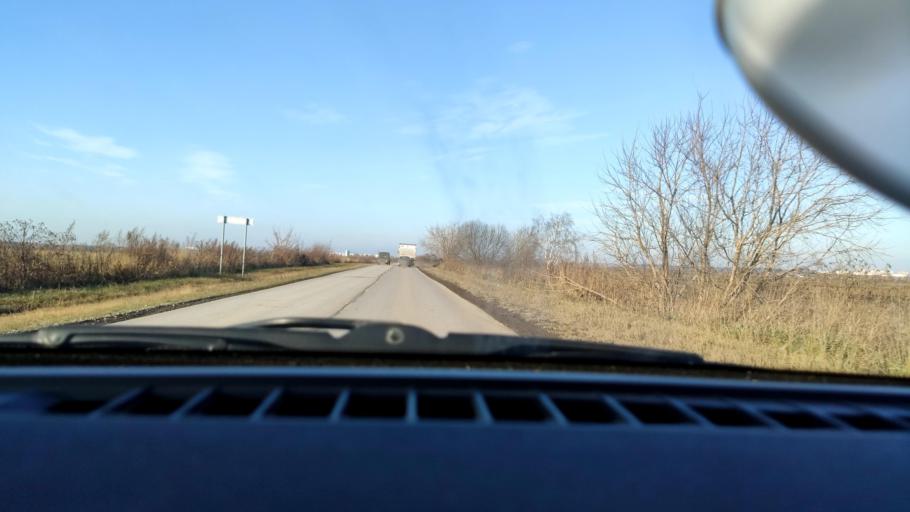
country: RU
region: Perm
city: Kondratovo
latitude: 57.9911
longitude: 56.0935
